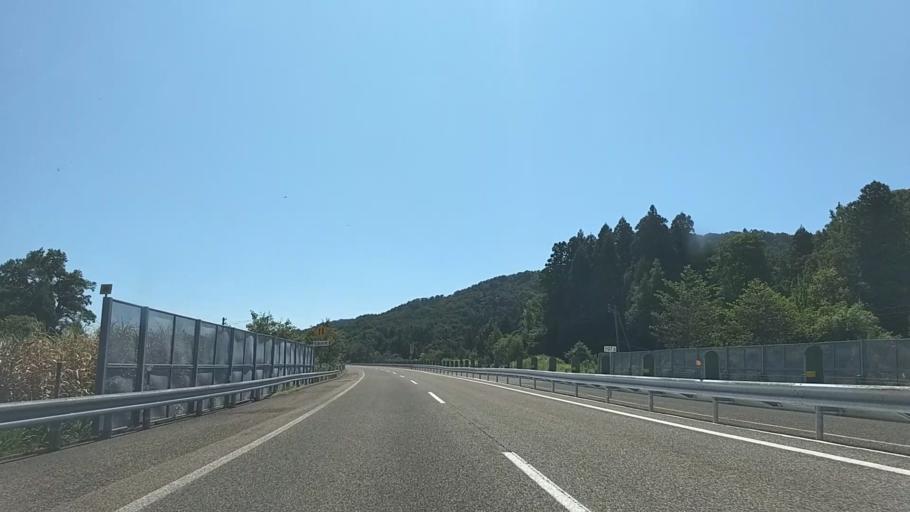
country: JP
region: Niigata
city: Joetsu
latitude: 37.0800
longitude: 138.2245
